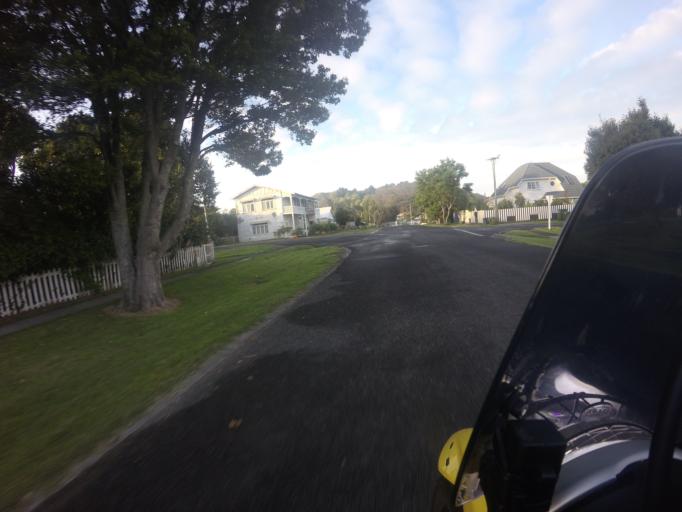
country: NZ
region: Gisborne
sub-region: Gisborne District
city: Gisborne
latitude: -38.6686
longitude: 178.0323
